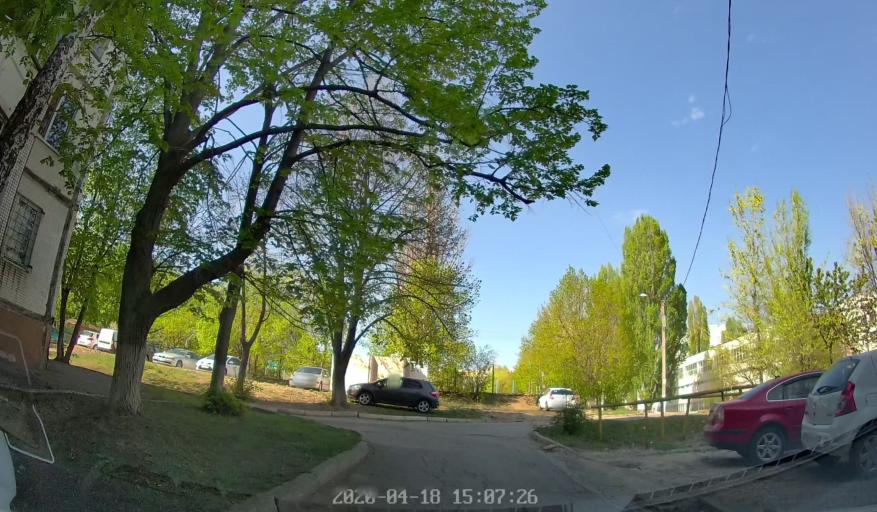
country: MD
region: Chisinau
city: Chisinau
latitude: 47.0447
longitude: 28.8853
